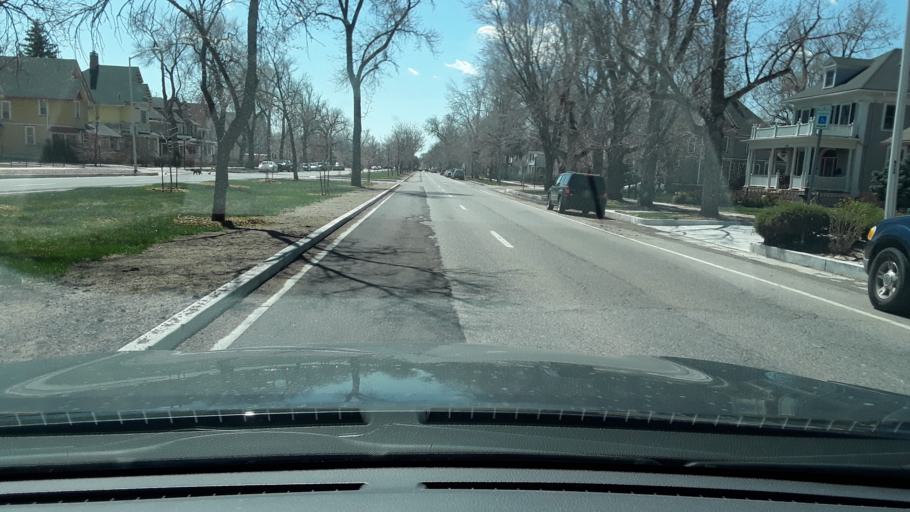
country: US
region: Colorado
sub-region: El Paso County
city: Colorado Springs
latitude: 38.8543
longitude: -104.8207
